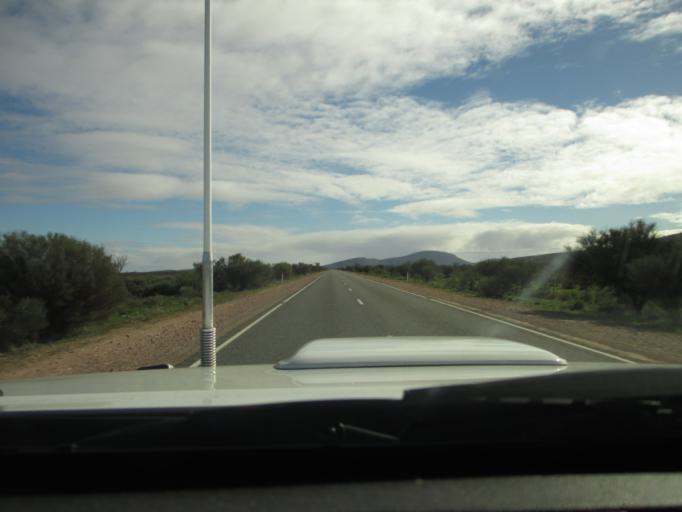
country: AU
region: South Australia
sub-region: Flinders Ranges
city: Quorn
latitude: -31.8526
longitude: 138.3979
